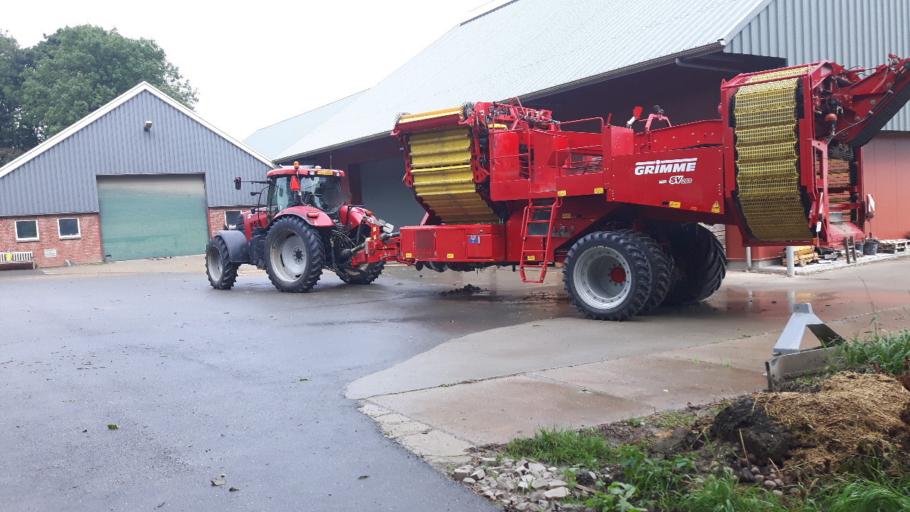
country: NL
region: Groningen
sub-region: Gemeente De Marne
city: Ulrum
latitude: 53.3364
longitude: 6.3620
